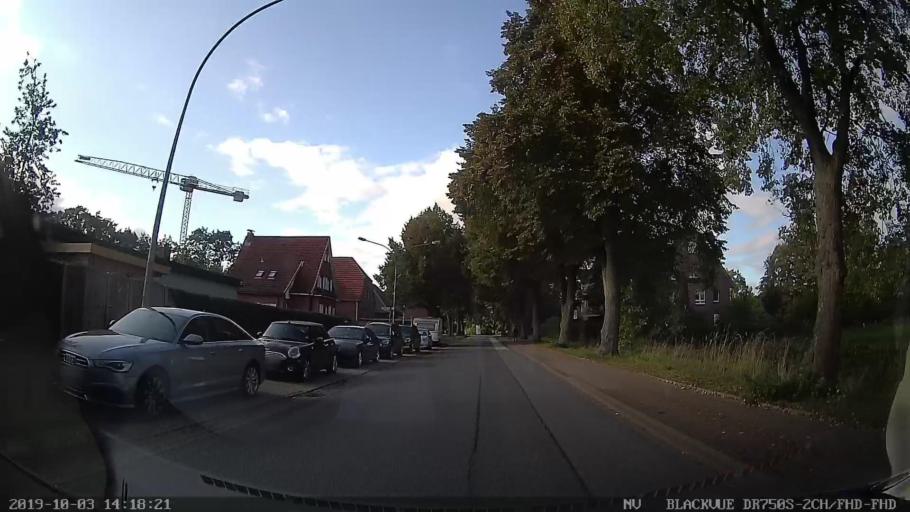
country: DE
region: Schleswig-Holstein
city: Pinneberg
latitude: 53.6652
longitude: 9.7986
